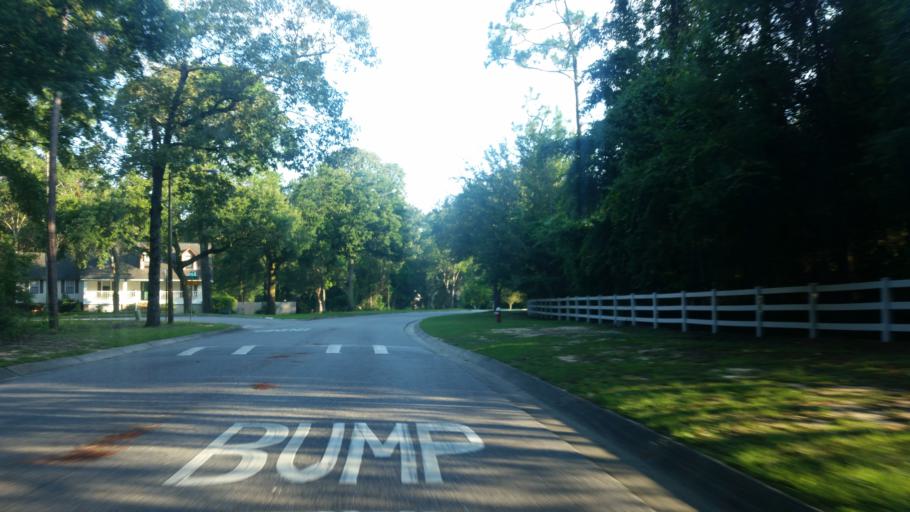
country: US
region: Florida
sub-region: Escambia County
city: Ensley
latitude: 30.5376
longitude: -87.2398
